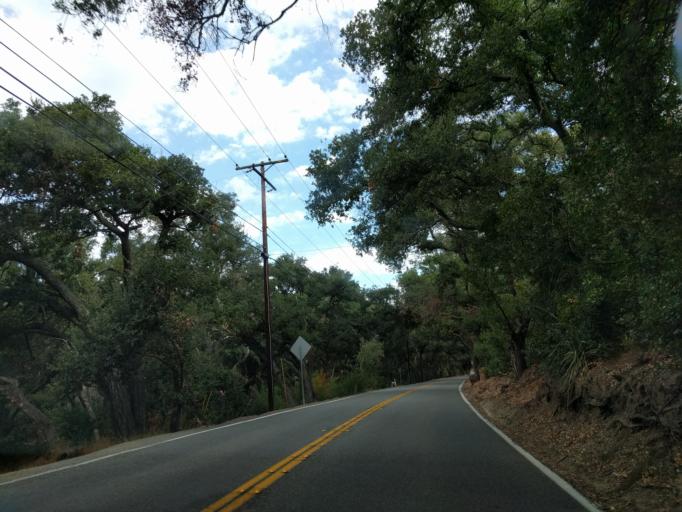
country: US
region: California
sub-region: Orange County
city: Trabuco Canyon
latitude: 33.6787
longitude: -117.6032
